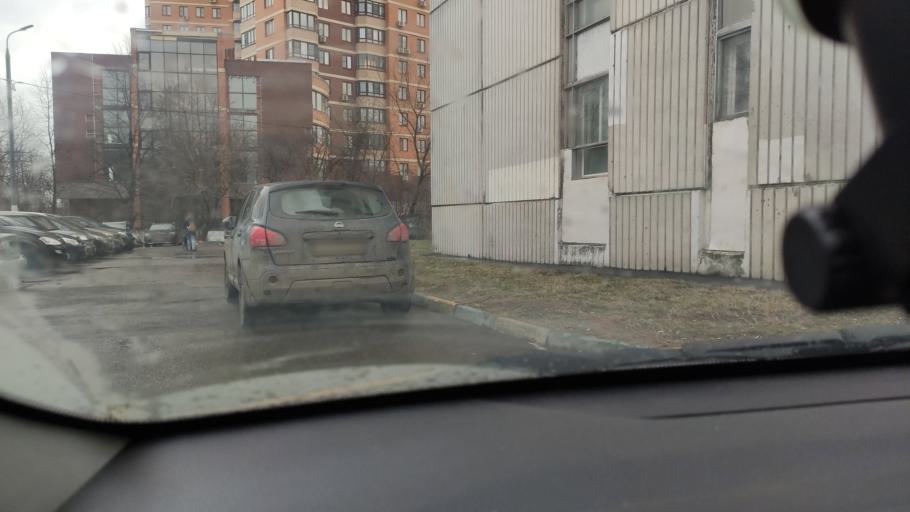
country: RU
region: Moscow
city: Chertanovo Yuzhnoye
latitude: 55.6164
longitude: 37.5986
